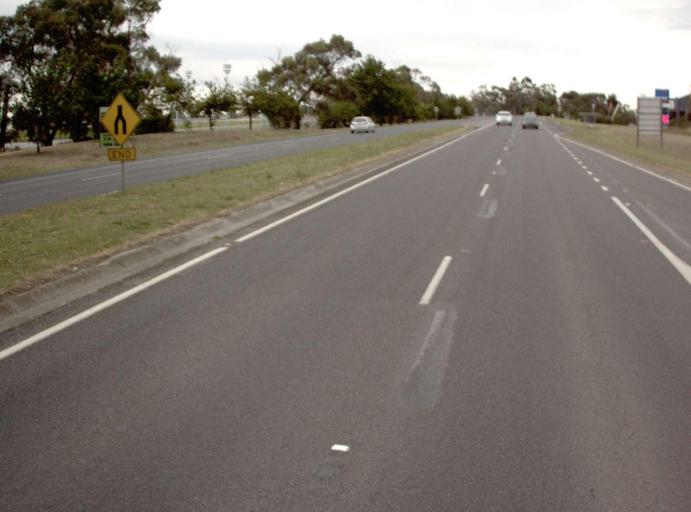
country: AU
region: Victoria
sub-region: Casey
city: Cranbourne
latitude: -38.1209
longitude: 145.2881
